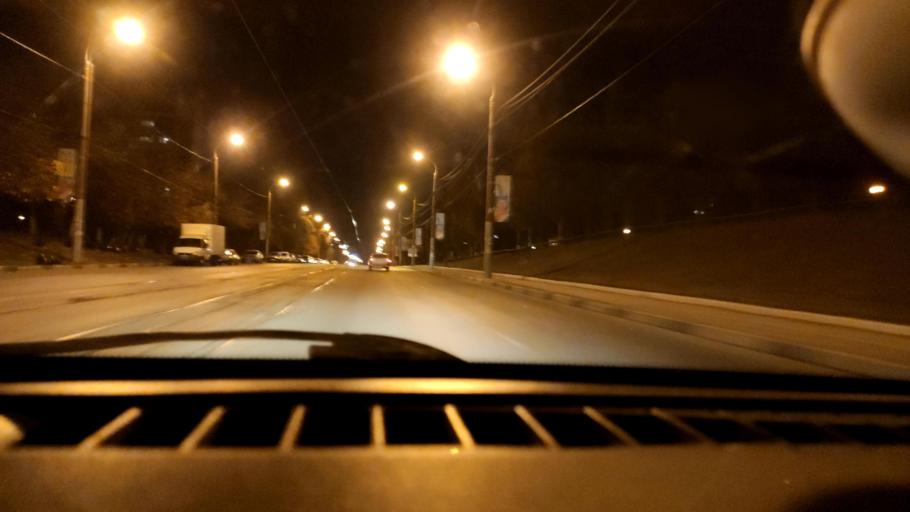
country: RU
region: Samara
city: Samara
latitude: 53.1920
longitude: 50.2038
